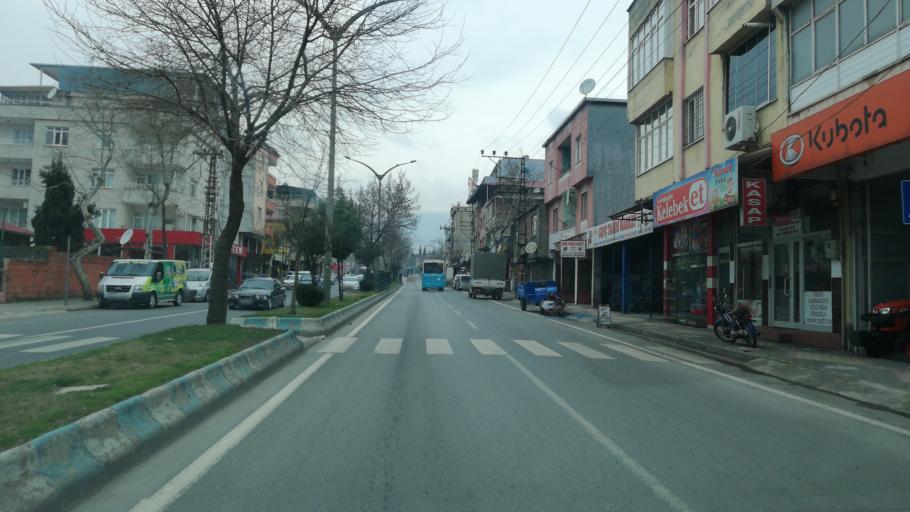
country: TR
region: Kahramanmaras
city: Kahramanmaras
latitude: 37.5680
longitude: 36.9480
